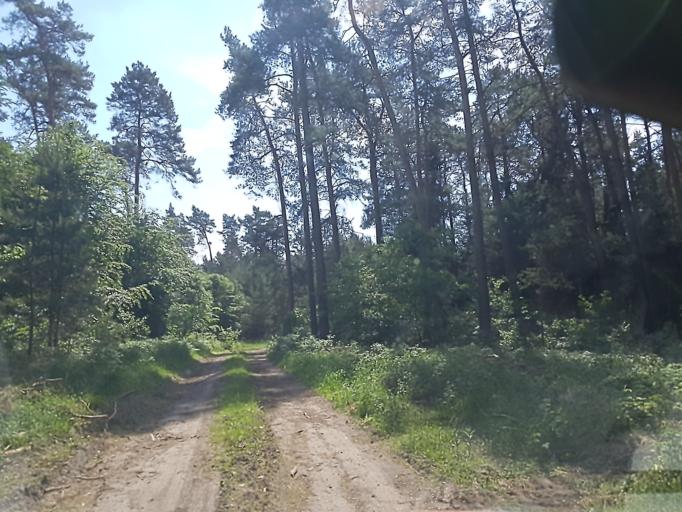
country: DE
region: Brandenburg
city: Gorzke
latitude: 52.1237
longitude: 12.3140
